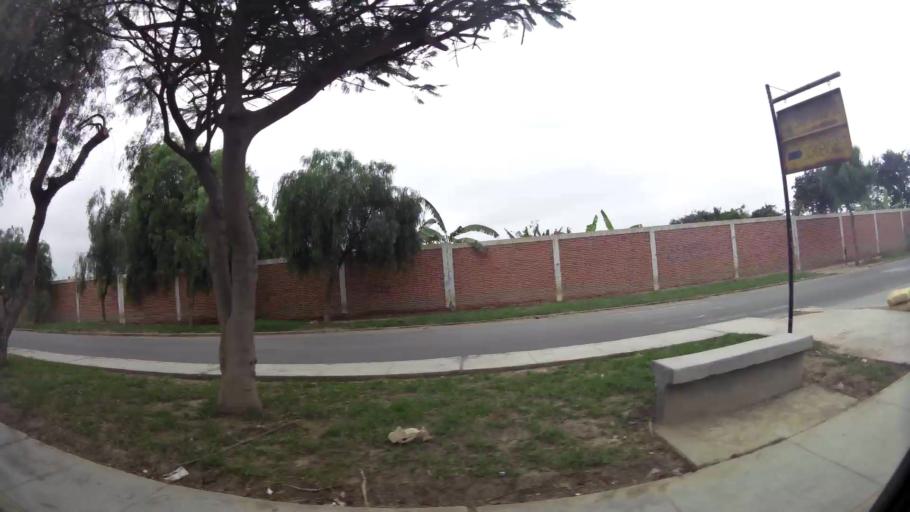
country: PE
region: La Libertad
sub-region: Provincia de Trujillo
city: Trujillo
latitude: -8.1146
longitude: -79.0426
